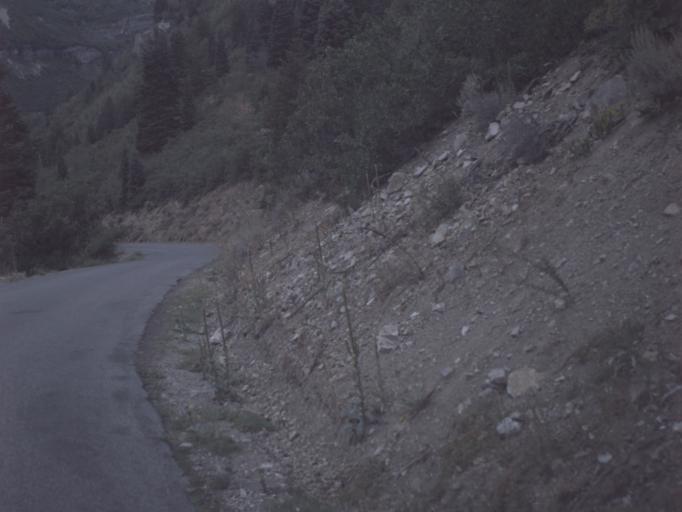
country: US
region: Utah
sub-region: Utah County
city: Lindon
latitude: 40.4081
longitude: -111.6031
